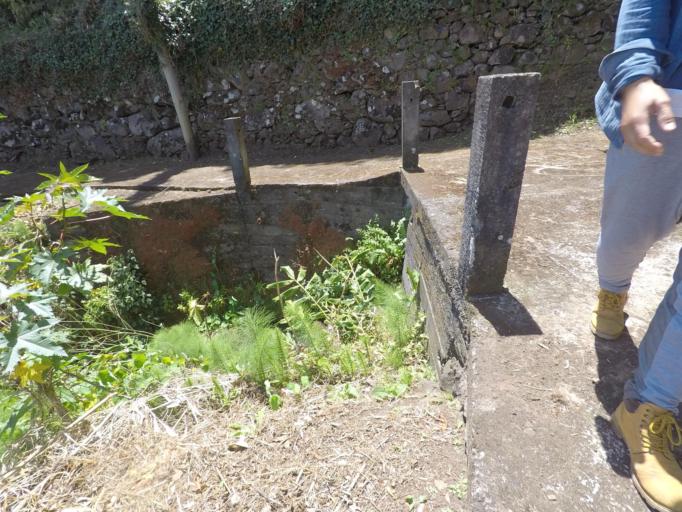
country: PT
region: Madeira
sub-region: Sao Vicente
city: Sao Vicente
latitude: 32.8224
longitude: -16.9776
